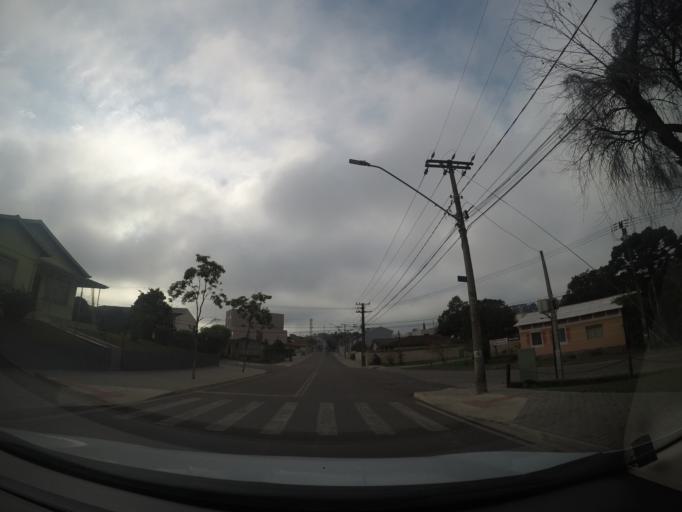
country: BR
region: Parana
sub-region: Colombo
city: Colombo
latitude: -25.2925
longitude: -49.2292
